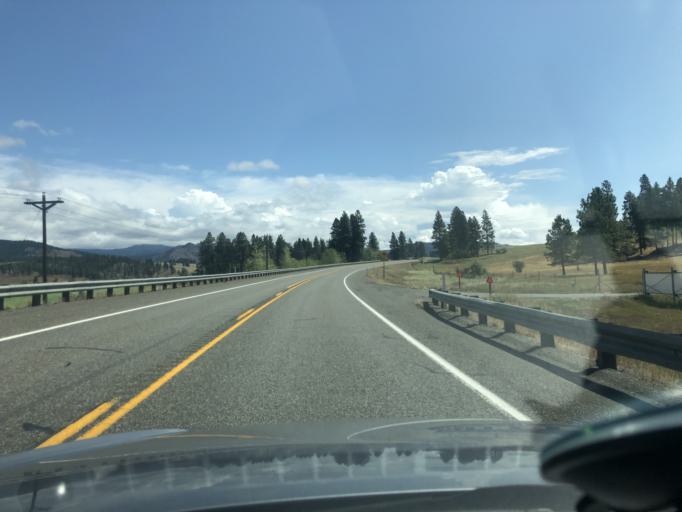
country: US
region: Washington
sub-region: Kittitas County
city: Cle Elum
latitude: 47.1963
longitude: -120.7779
